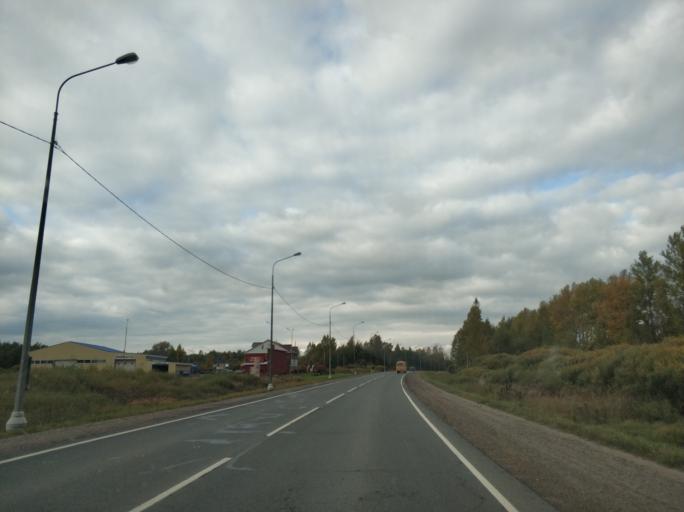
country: RU
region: Pskov
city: Ostrov
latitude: 57.3146
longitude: 28.3629
